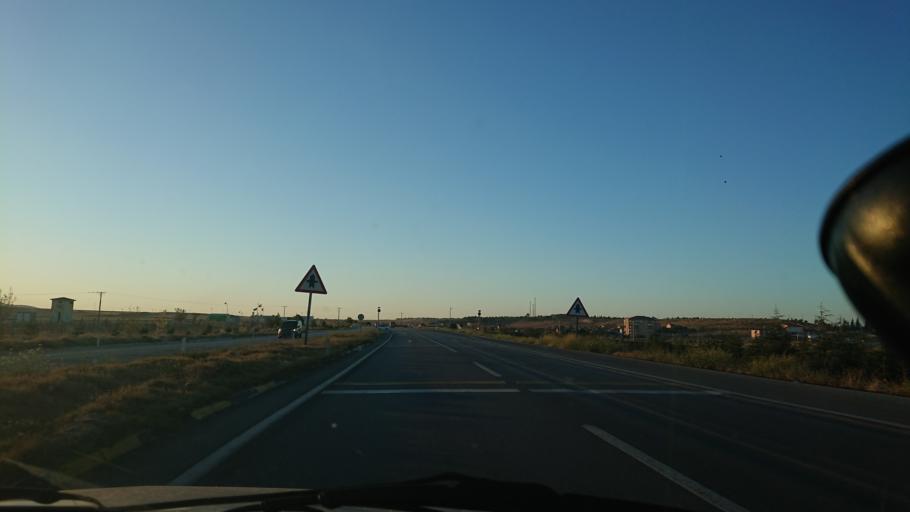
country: TR
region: Eskisehir
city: Mahmudiye
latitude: 39.4865
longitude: 30.9840
